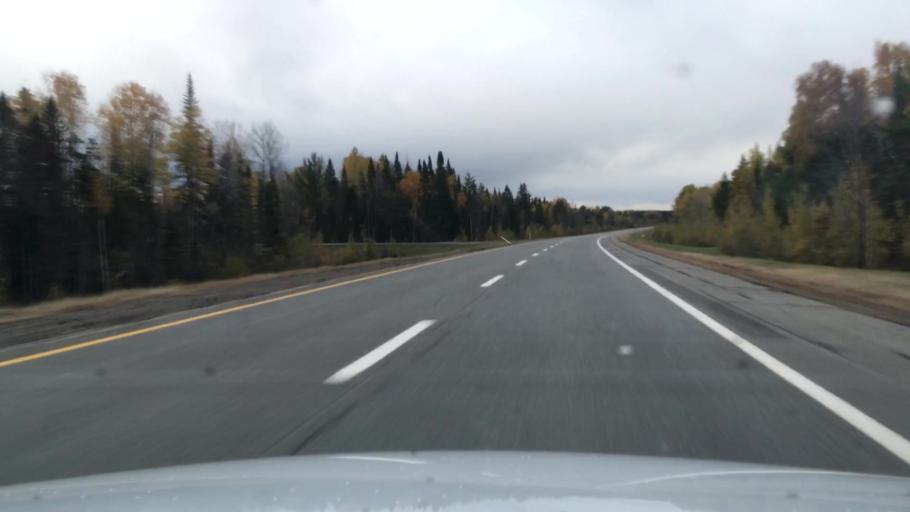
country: US
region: Maine
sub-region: Penobscot County
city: Greenbush
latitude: 45.1232
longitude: -68.6955
